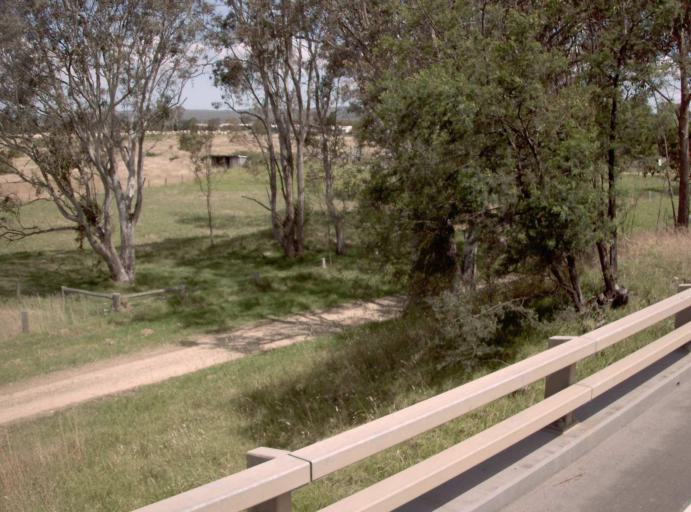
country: AU
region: Victoria
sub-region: Wellington
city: Heyfield
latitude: -38.1481
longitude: 146.7905
